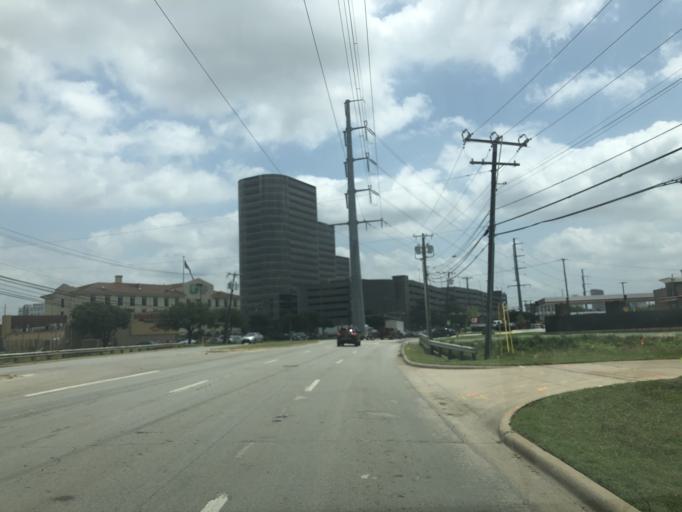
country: US
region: Texas
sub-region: Dallas County
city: Dallas
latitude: 32.8092
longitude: -96.8529
